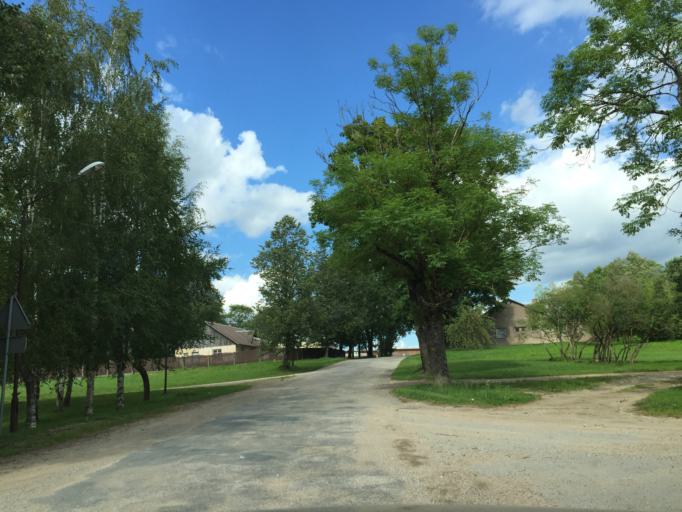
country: LV
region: Malpils
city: Malpils
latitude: 56.8576
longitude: 25.0190
